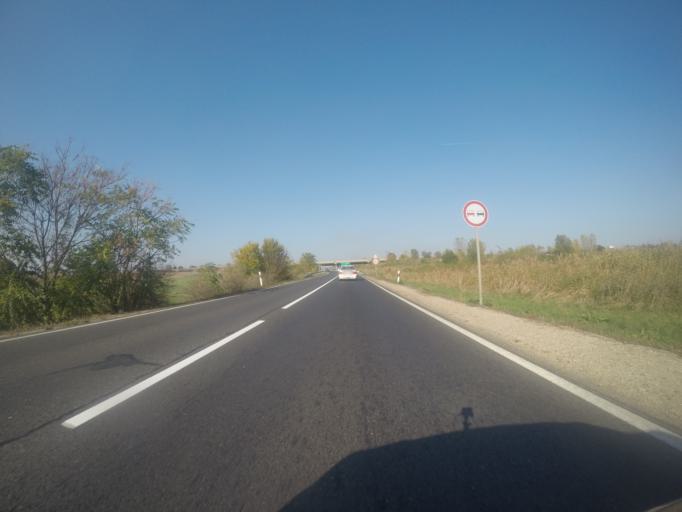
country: HU
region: Fejer
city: Baracs
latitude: 46.9081
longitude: 18.9257
